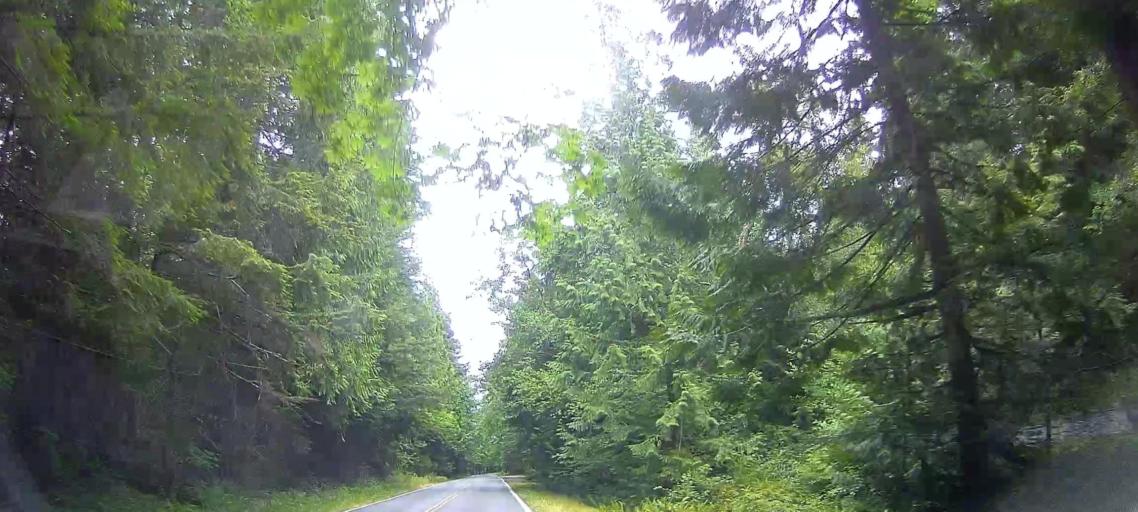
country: US
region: Washington
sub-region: Skagit County
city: Anacortes
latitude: 48.4669
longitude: -122.6310
